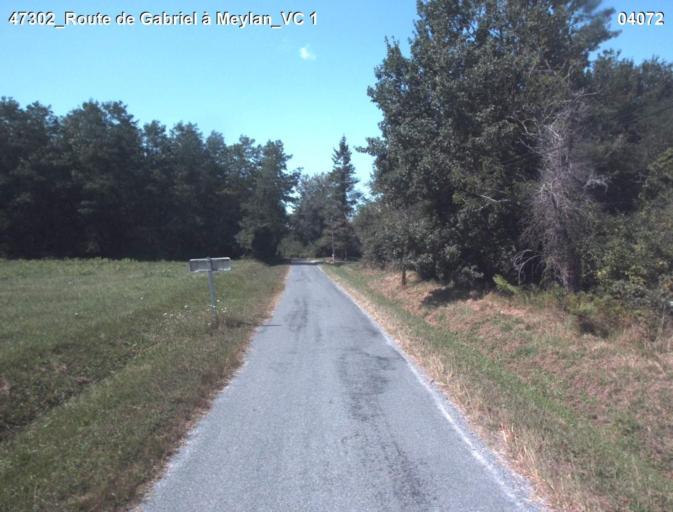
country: FR
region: Aquitaine
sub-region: Departement des Landes
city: Gabarret
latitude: 44.0774
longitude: 0.1164
